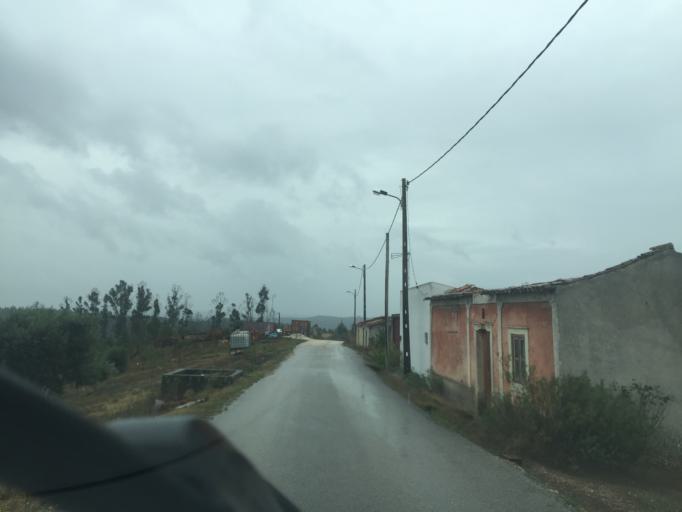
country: PT
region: Coimbra
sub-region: Figueira da Foz
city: Lavos
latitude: 40.0775
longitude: -8.7891
